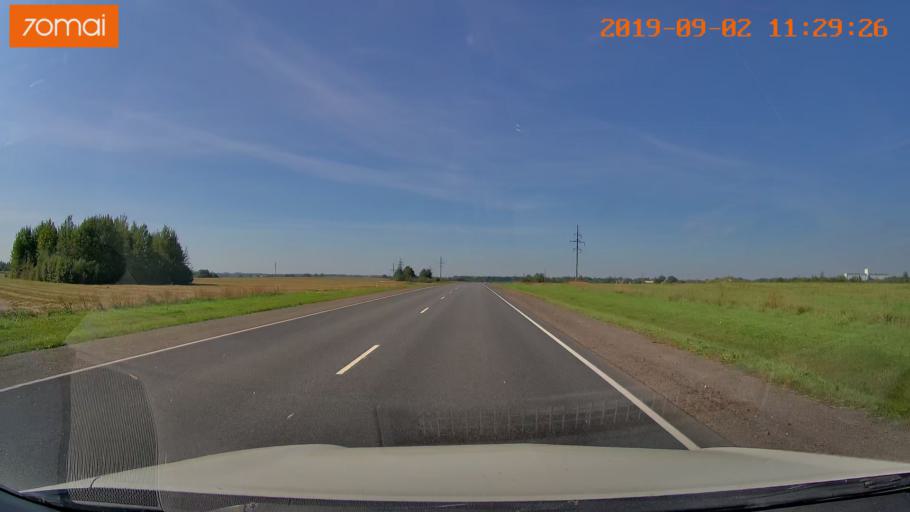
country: RU
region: Smolensk
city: Roslavl'
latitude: 53.9892
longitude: 32.8603
